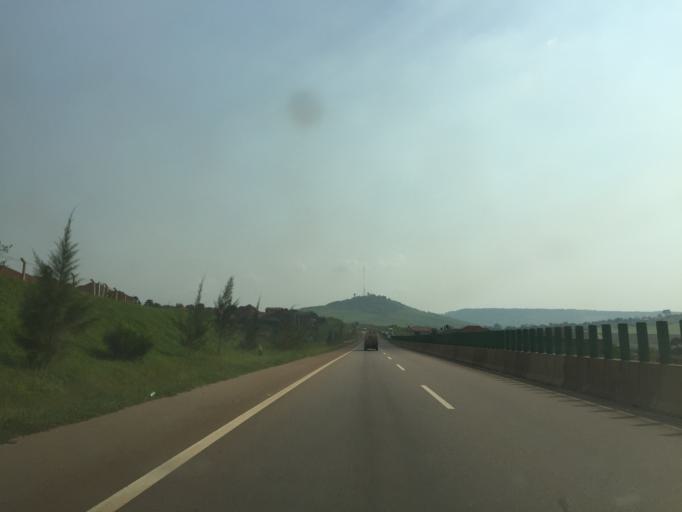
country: UG
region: Central Region
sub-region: Wakiso District
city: Kajansi
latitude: 0.2388
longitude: 32.5240
